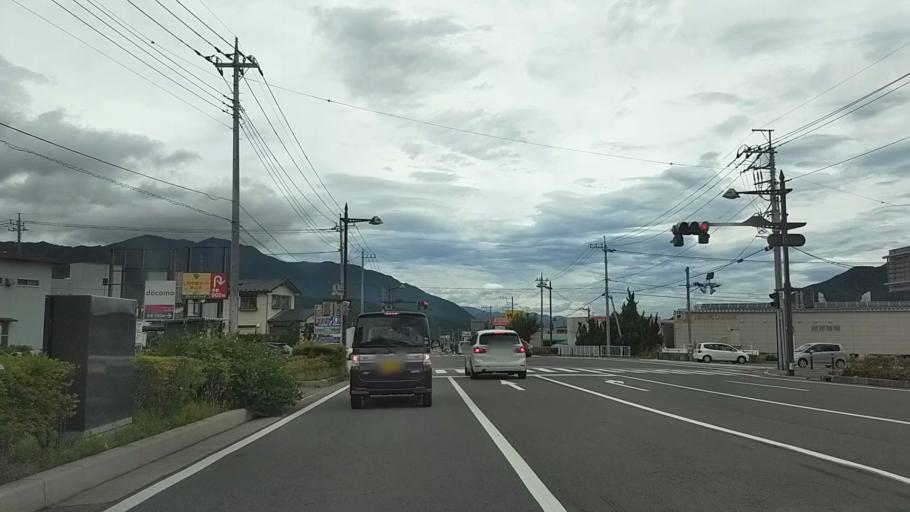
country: JP
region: Yamanashi
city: Fujikawaguchiko
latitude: 35.4771
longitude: 138.8086
